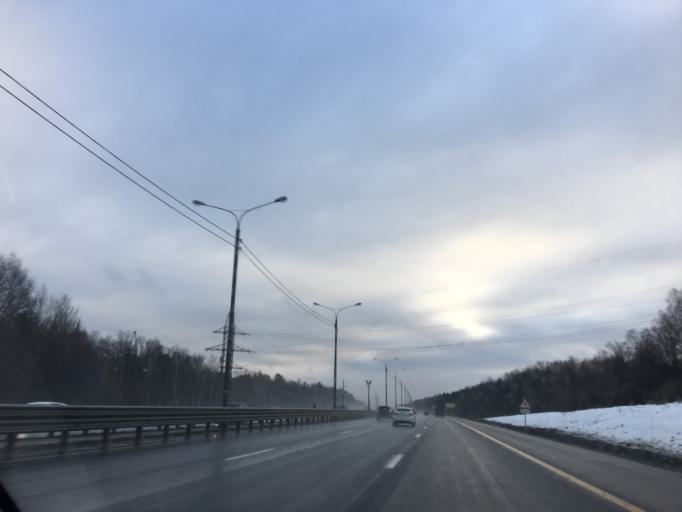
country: RU
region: Moskovskaya
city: L'vovskiy
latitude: 55.3041
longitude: 37.5486
